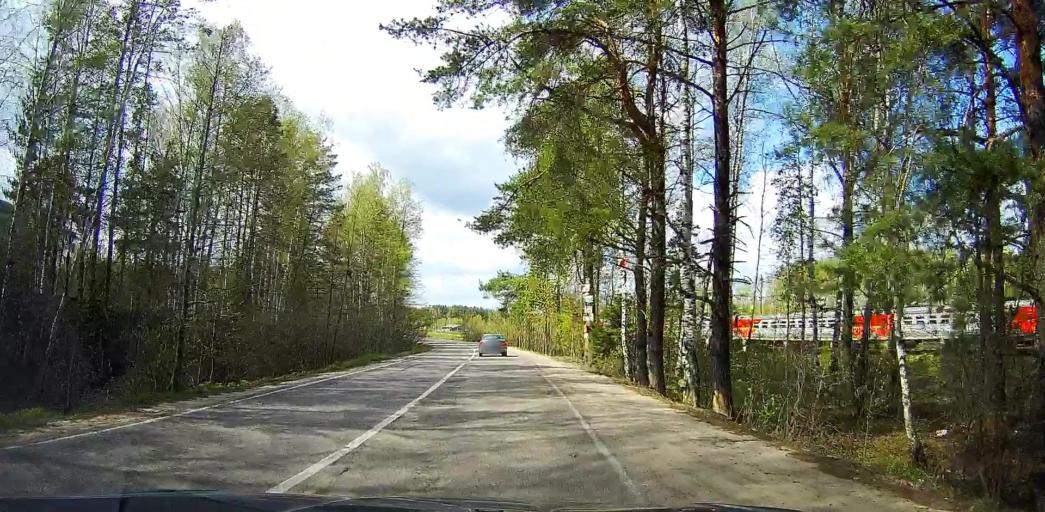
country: RU
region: Moskovskaya
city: Davydovo
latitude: 55.5717
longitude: 38.8226
